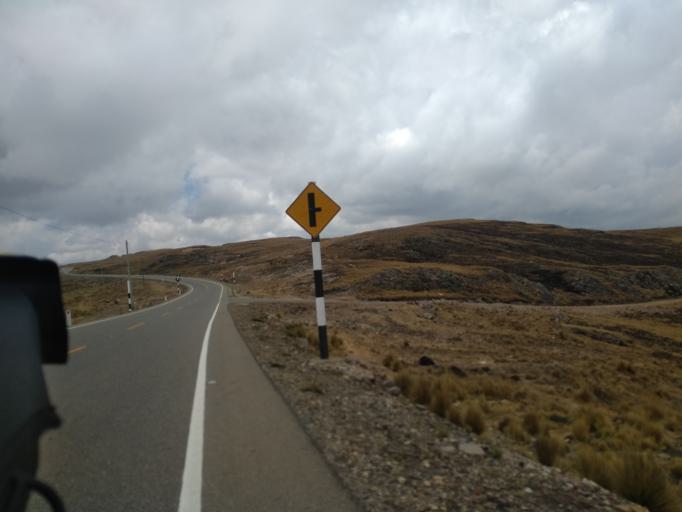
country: PE
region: La Libertad
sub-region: Provincia de Santiago de Chuco
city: Quiruvilca
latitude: -7.9615
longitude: -78.1967
